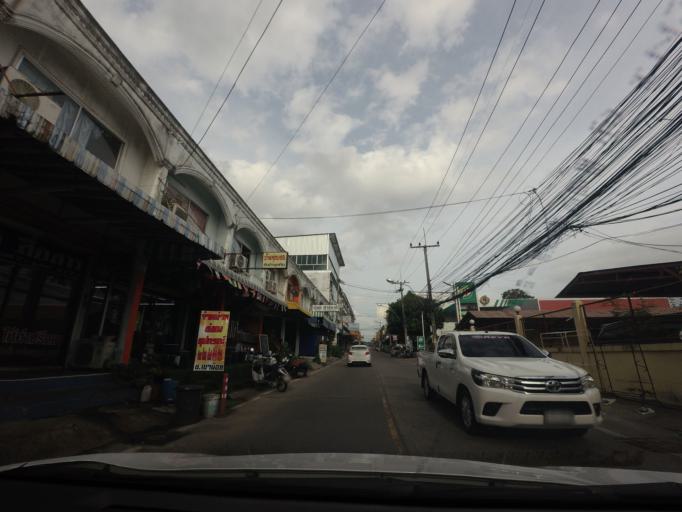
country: TH
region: Chon Buri
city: Phatthaya
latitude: 12.9268
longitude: 100.8999
